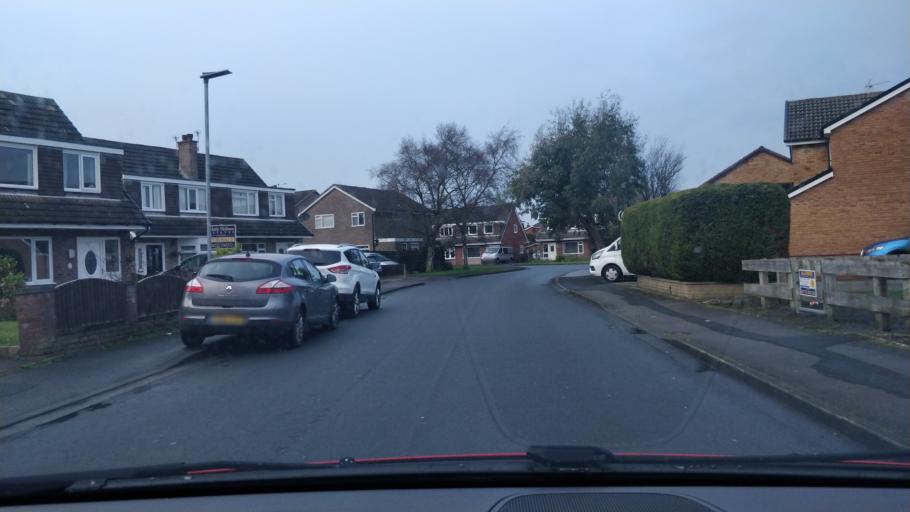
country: GB
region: England
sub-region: Lancashire
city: Preston
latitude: 53.7423
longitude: -2.7356
